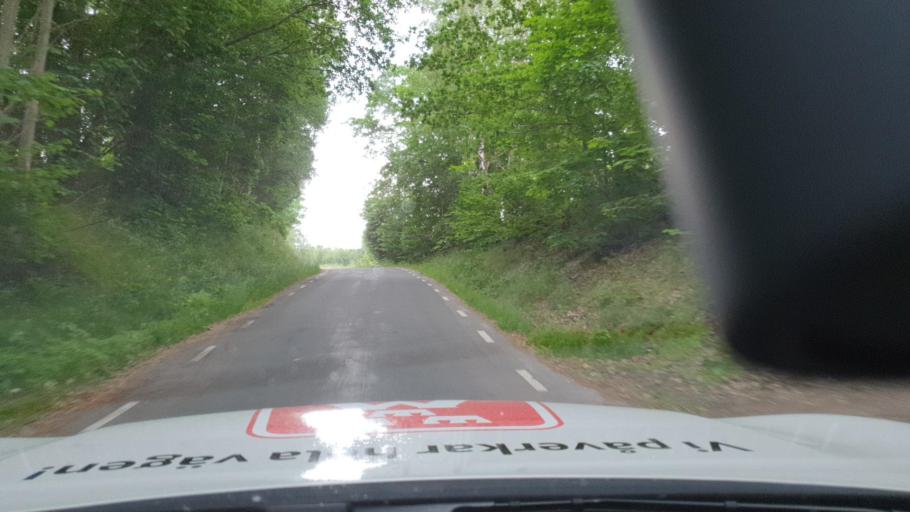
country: SE
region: Vaestra Goetaland
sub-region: Hjo Kommun
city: Hjo
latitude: 58.1753
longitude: 14.1924
